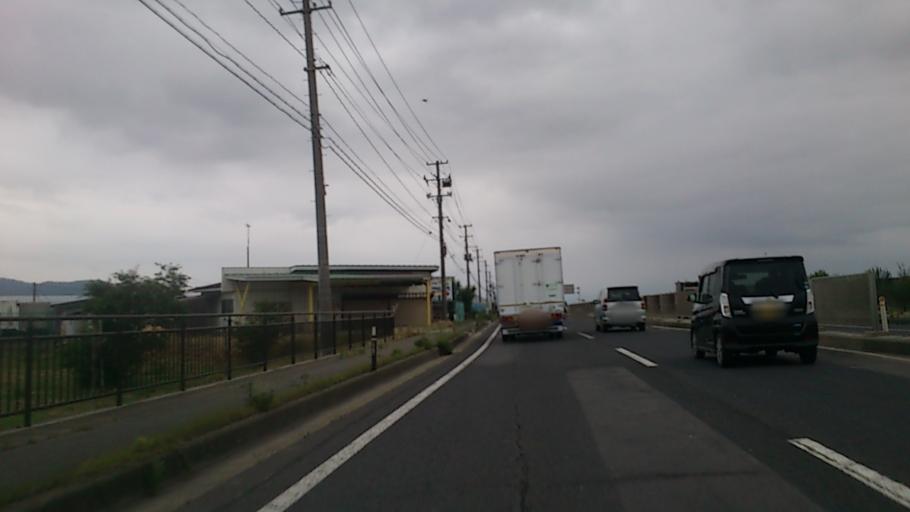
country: JP
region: Yamagata
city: Higashine
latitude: 38.4175
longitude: 140.3753
